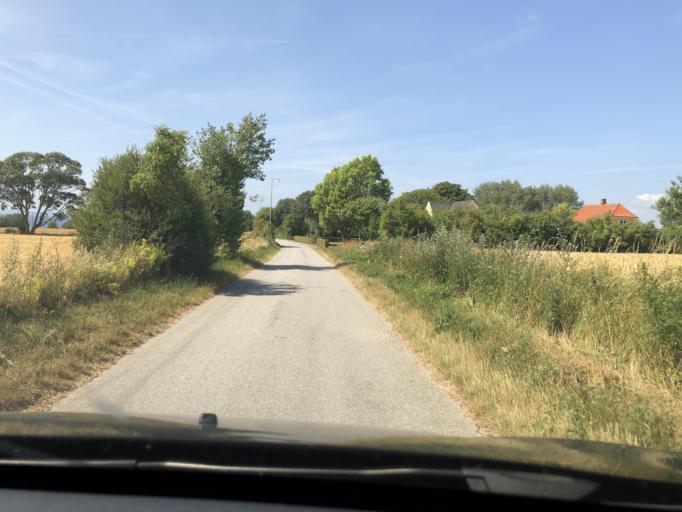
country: DK
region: South Denmark
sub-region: AEro Kommune
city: AEroskobing
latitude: 54.8963
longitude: 10.2885
